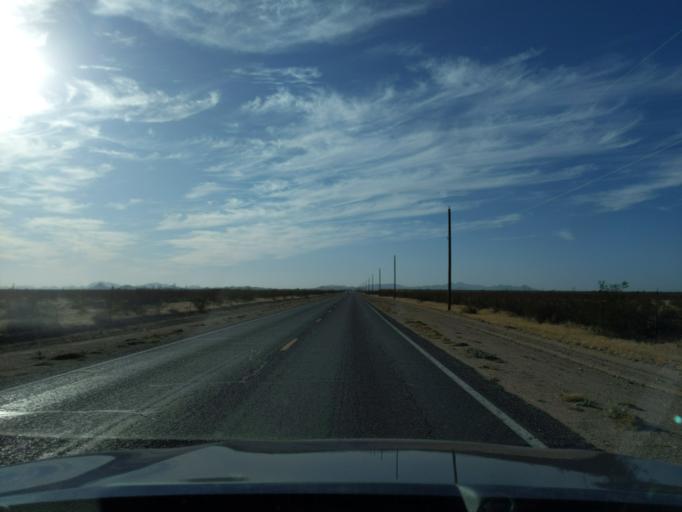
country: US
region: Arizona
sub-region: Pinal County
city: Florence
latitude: 33.1183
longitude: -111.3766
